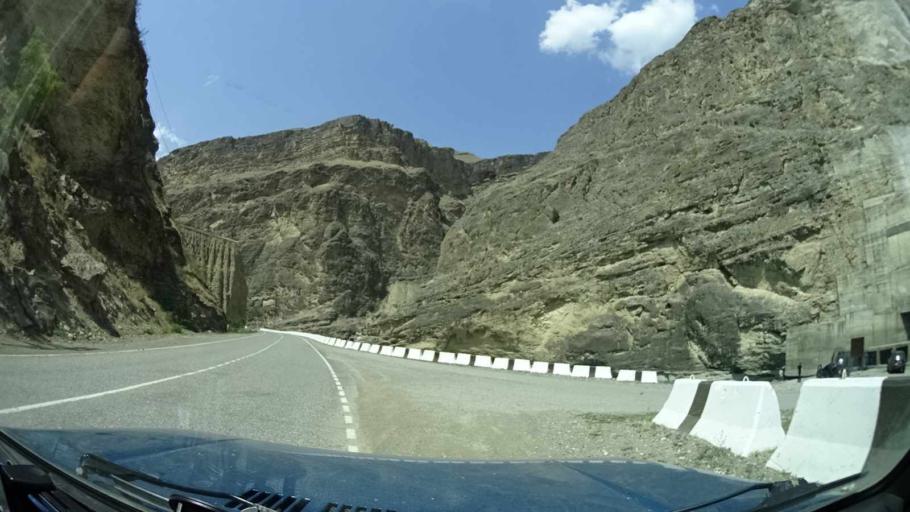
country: RU
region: Dagestan
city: Shamil'kala
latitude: 42.6980
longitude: 46.8273
